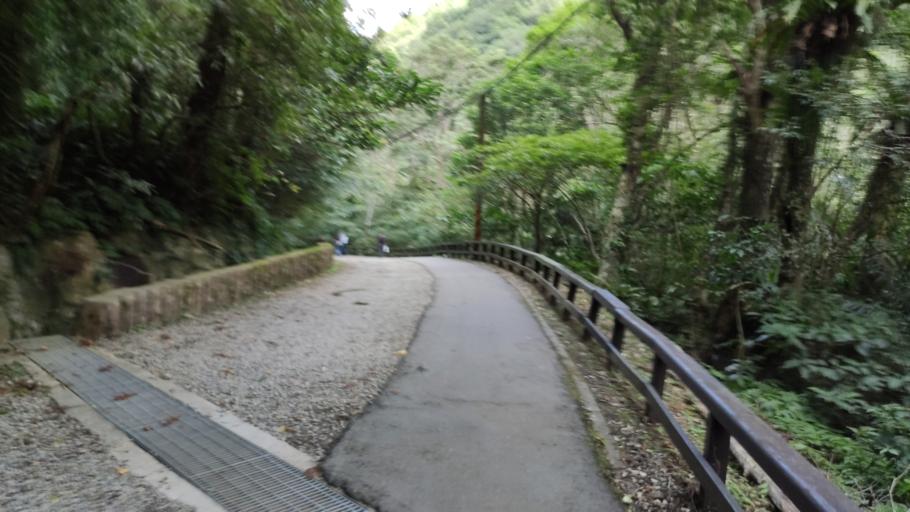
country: TW
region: Taiwan
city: Daxi
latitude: 24.8262
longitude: 121.4482
